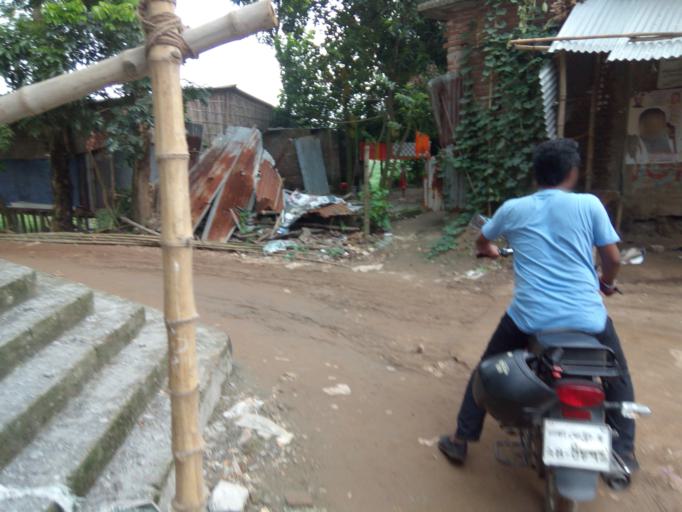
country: BD
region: Dhaka
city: Paltan
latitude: 23.7387
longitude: 90.4620
